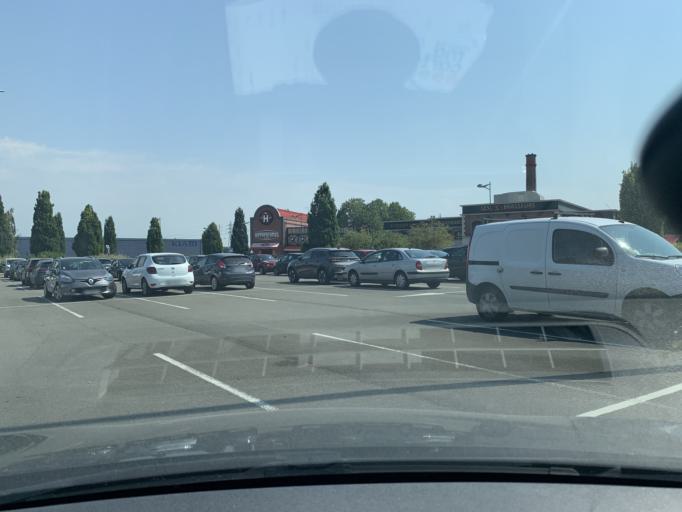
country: FR
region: Nord-Pas-de-Calais
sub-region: Departement du Pas-de-Calais
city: Henin-Beaumont
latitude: 50.4070
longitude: 2.9760
